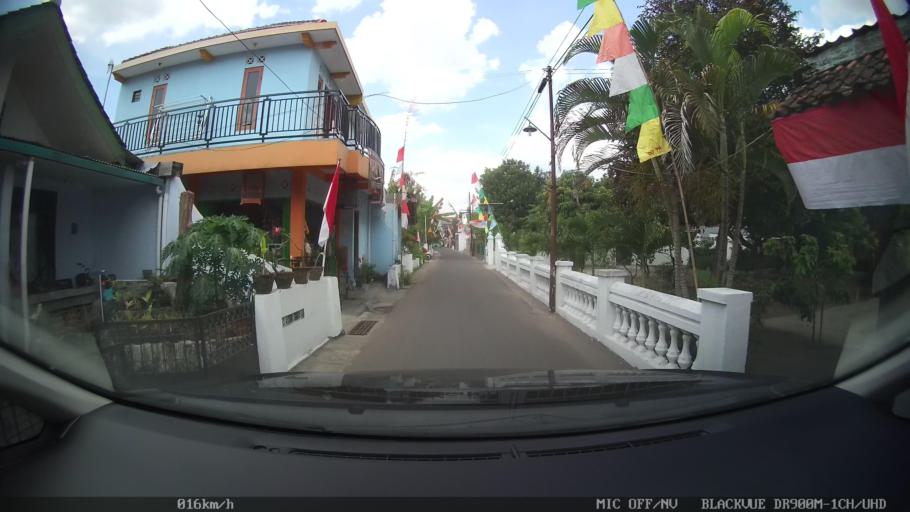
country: ID
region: Daerah Istimewa Yogyakarta
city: Kasihan
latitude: -7.8148
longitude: 110.3463
